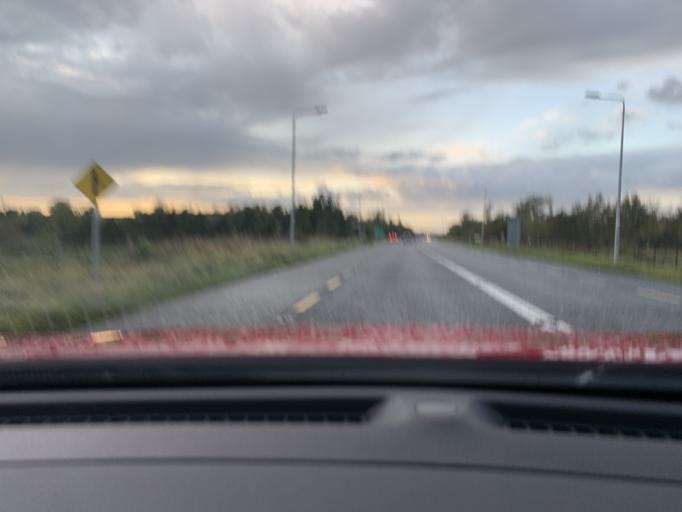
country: IE
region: Connaught
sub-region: County Leitrim
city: Carrick-on-Shannon
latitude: 53.9449
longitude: -8.1166
